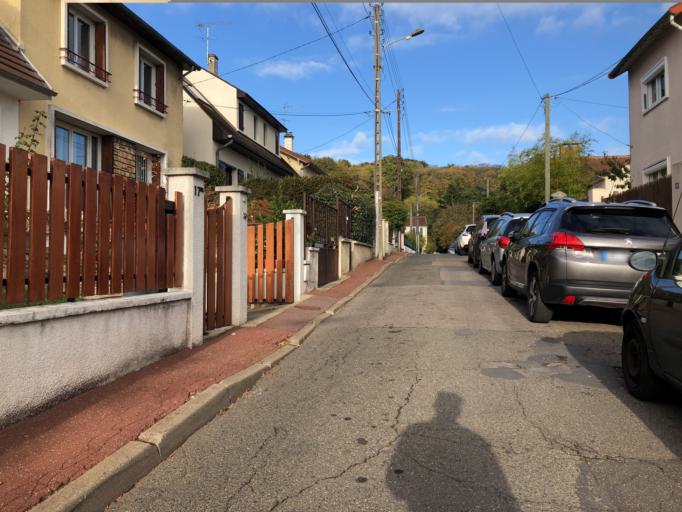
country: FR
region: Ile-de-France
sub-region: Departement des Hauts-de-Seine
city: Chaville
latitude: 48.8090
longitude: 2.1793
